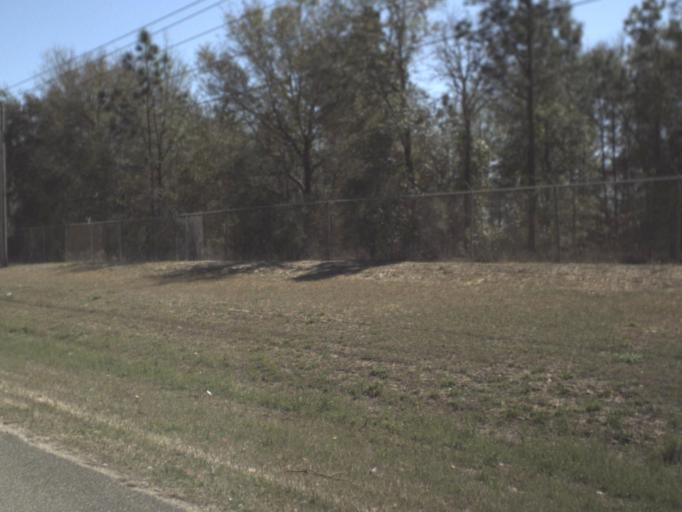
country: US
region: Florida
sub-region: Leon County
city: Tallahassee
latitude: 30.3893
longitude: -84.3157
